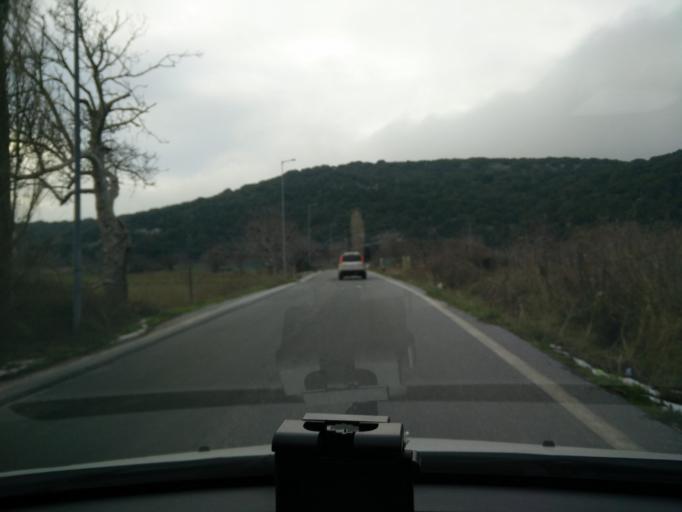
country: GR
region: Crete
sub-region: Nomos Irakleiou
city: Mokhos
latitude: 35.2033
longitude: 25.4776
